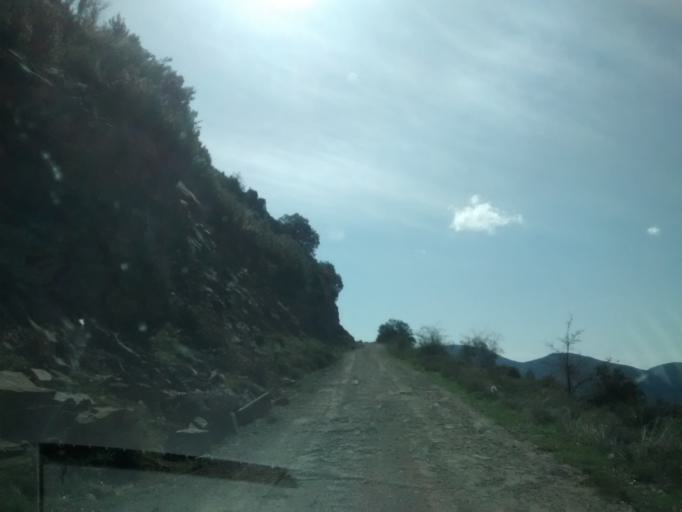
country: ES
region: Aragon
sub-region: Provincia de Huesca
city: Arguis
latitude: 42.3266
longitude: -0.3957
